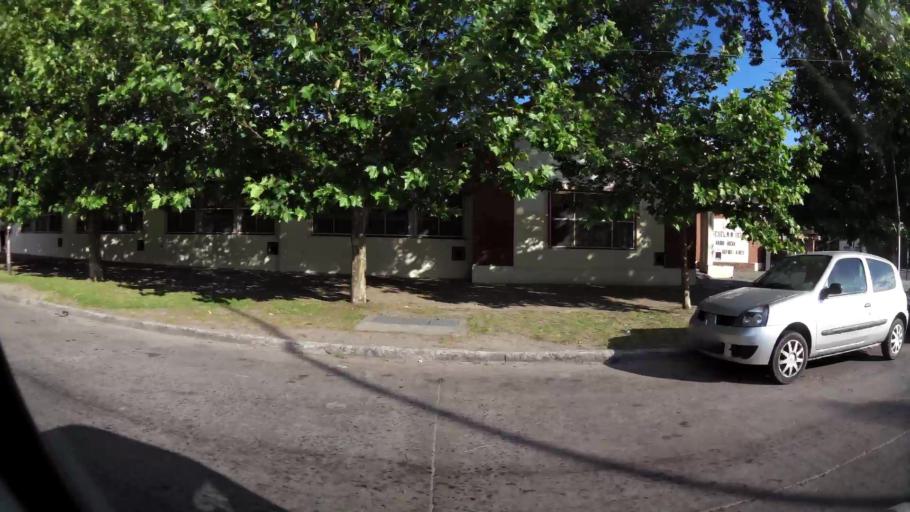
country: AR
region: Buenos Aires
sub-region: Partido de La Plata
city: La Plata
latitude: -34.9003
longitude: -57.9687
